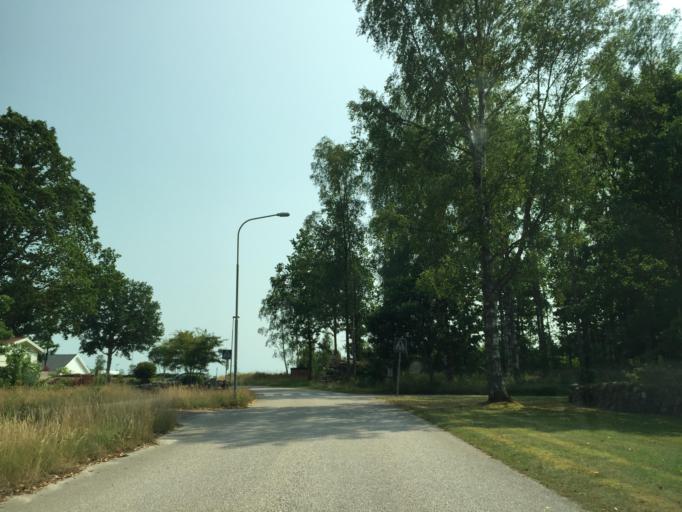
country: SE
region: Vaestra Goetaland
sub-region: Lilla Edets Kommun
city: Lilla Edet
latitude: 58.1787
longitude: 12.1019
